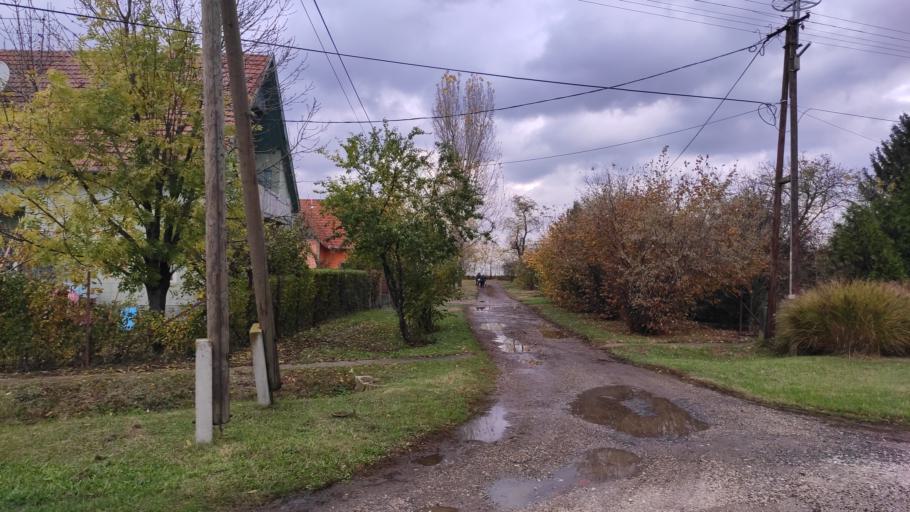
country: HU
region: Bekes
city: Mezobereny
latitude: 46.7642
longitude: 21.0404
